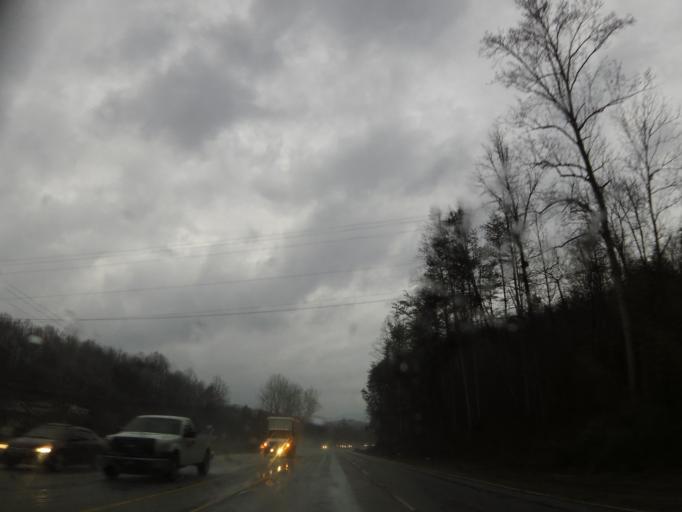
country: US
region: South Carolina
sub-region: Greenville County
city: Slater-Marietta
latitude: 35.0783
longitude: -82.4455
